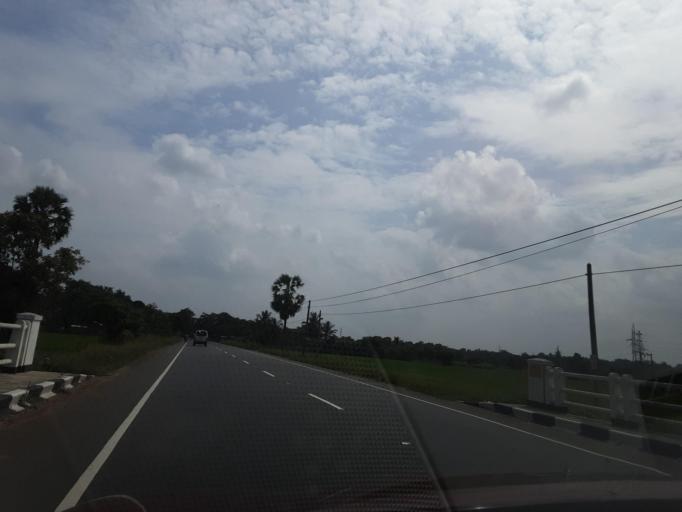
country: LK
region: North Central
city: Anuradhapura
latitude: 8.5074
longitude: 80.5073
